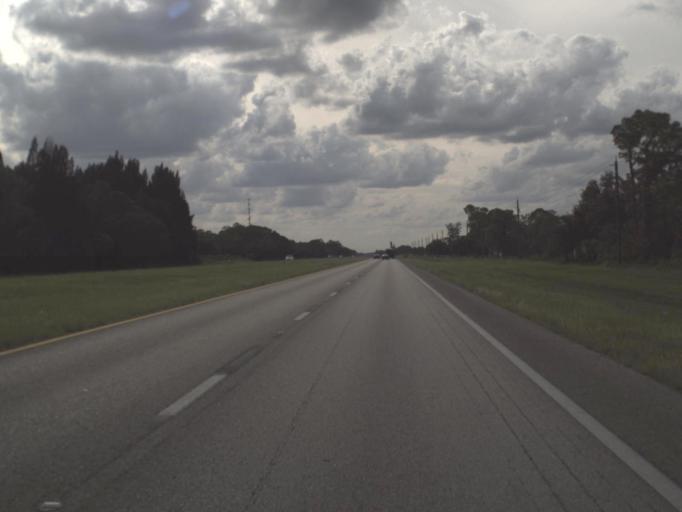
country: US
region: Florida
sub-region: Lee County
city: Alva
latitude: 26.7098
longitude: -81.5446
